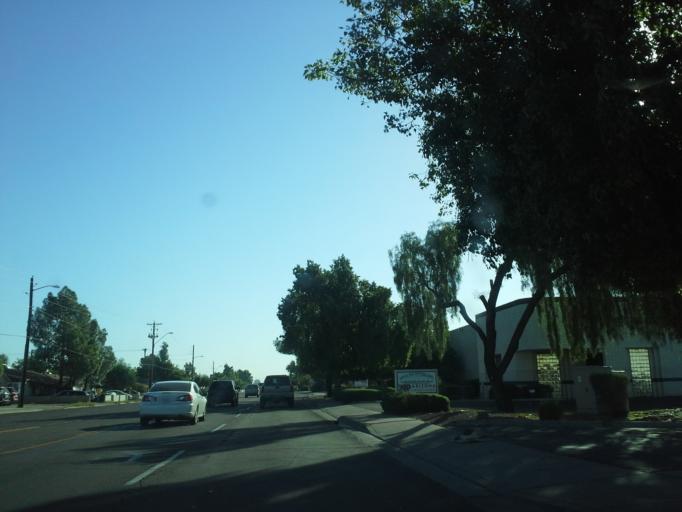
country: US
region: Arizona
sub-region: Maricopa County
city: Glendale
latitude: 33.4804
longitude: -112.1409
